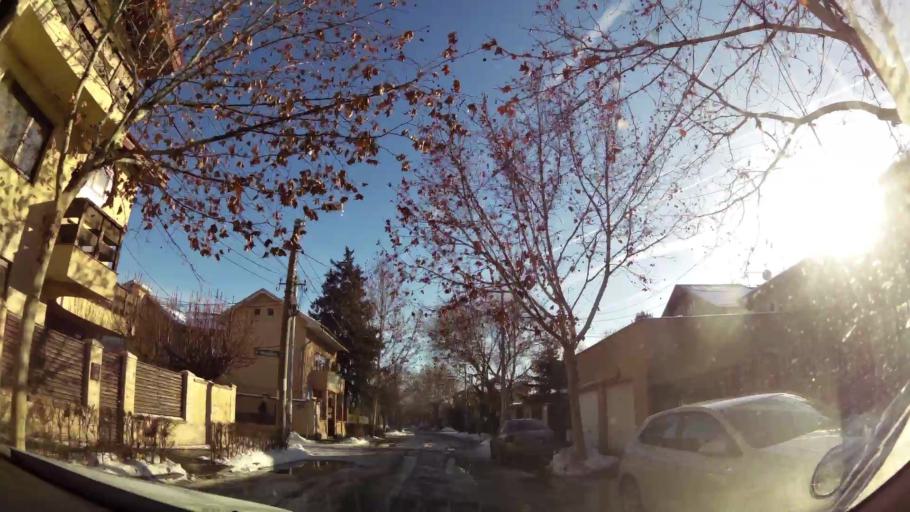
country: RO
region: Ilfov
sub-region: Comuna Fundeni-Dobroesti
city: Fundeni
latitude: 44.4781
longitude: 26.1527
